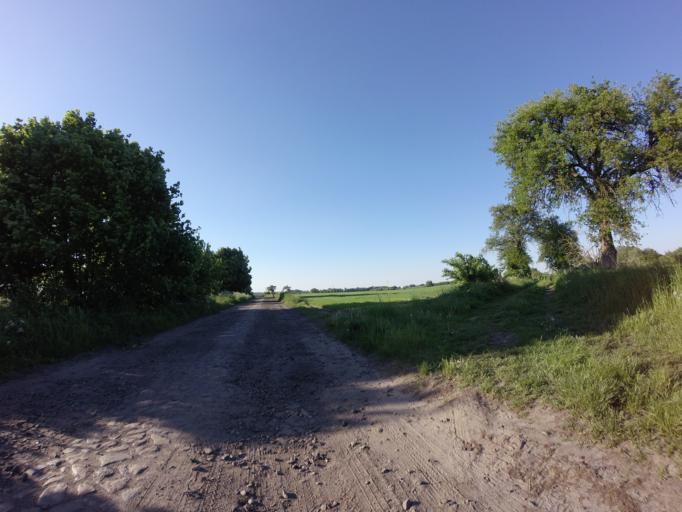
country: PL
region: West Pomeranian Voivodeship
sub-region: Powiat choszczenski
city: Choszczno
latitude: 53.1342
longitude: 15.4398
